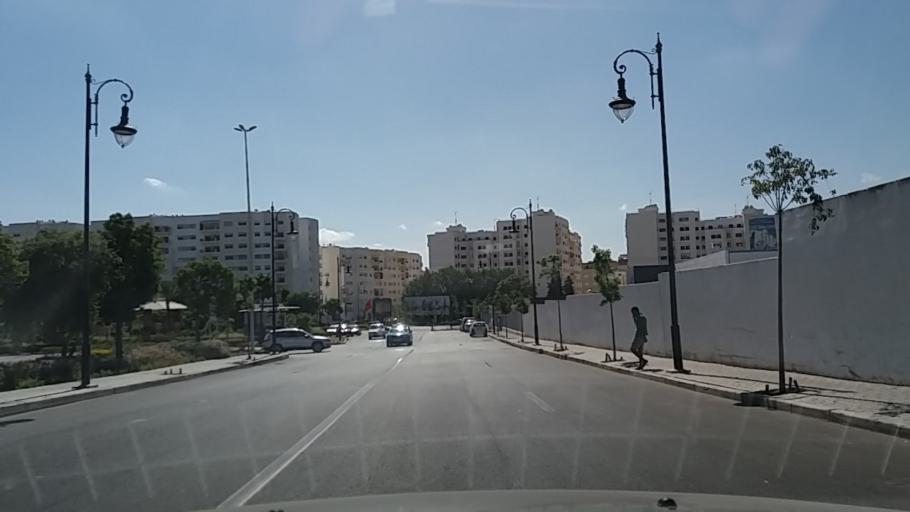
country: MA
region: Tanger-Tetouan
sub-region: Tanger-Assilah
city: Tangier
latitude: 35.7448
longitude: -5.8457
